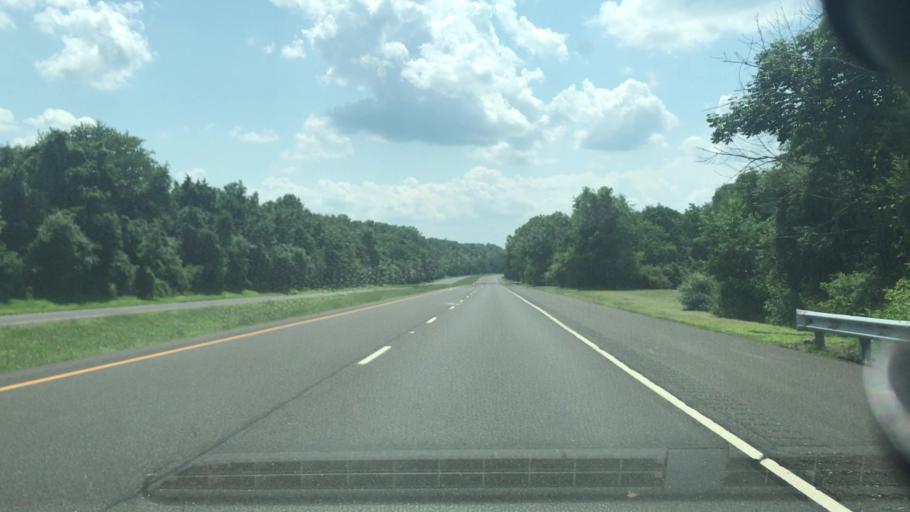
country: US
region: New Jersey
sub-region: Hunterdon County
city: Lambertville
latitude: 40.3968
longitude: -74.9232
